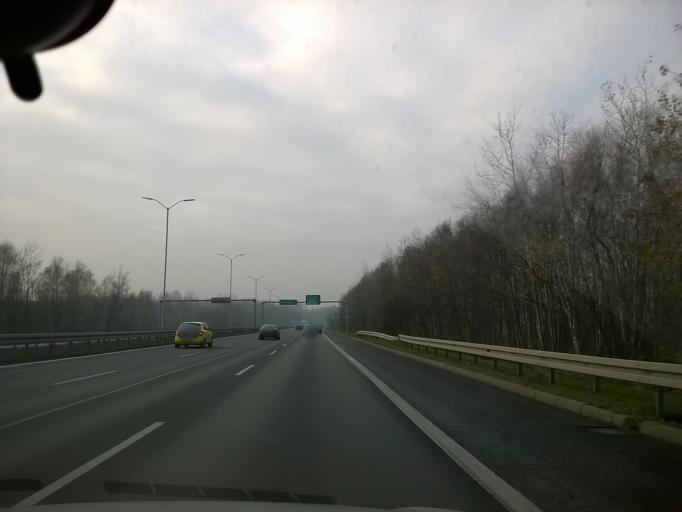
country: PL
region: Silesian Voivodeship
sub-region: Swietochlowice
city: Swietochlowice
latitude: 50.2965
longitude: 18.8925
